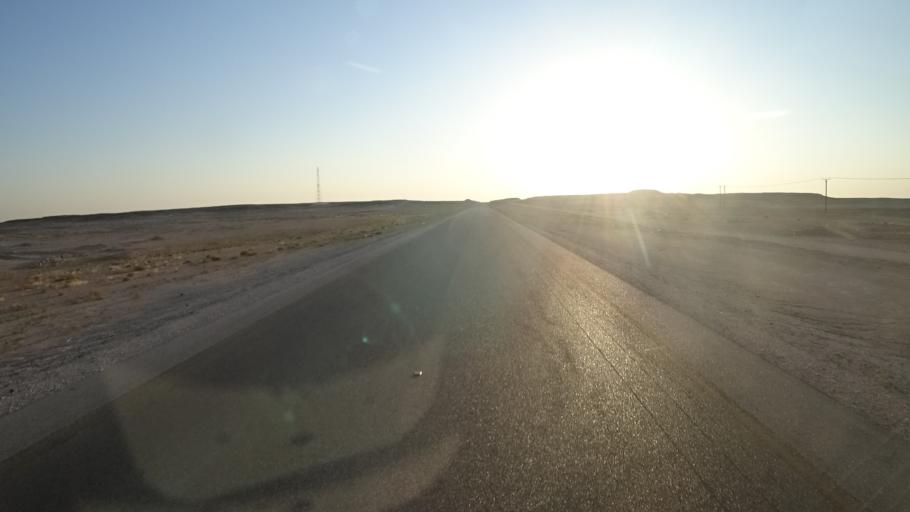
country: OM
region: Zufar
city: Salalah
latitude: 17.5420
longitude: 53.4183
